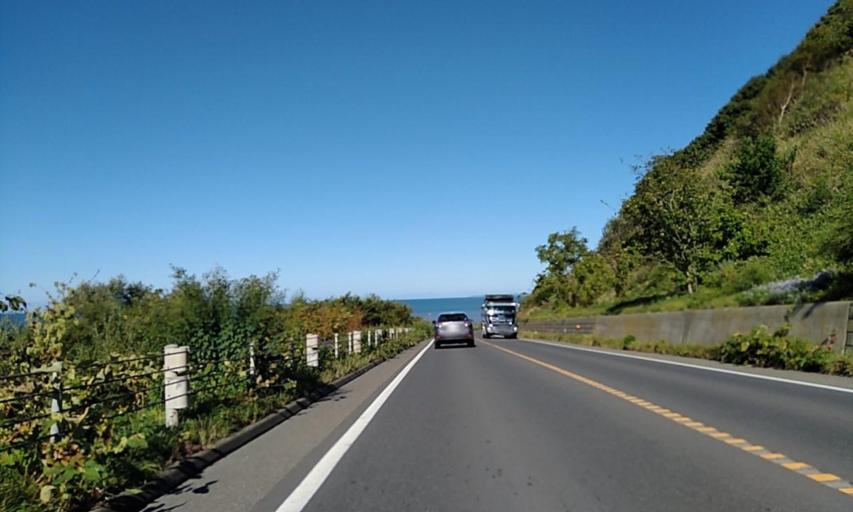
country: JP
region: Hokkaido
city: Shizunai-furukawacho
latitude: 42.3840
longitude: 142.2743
